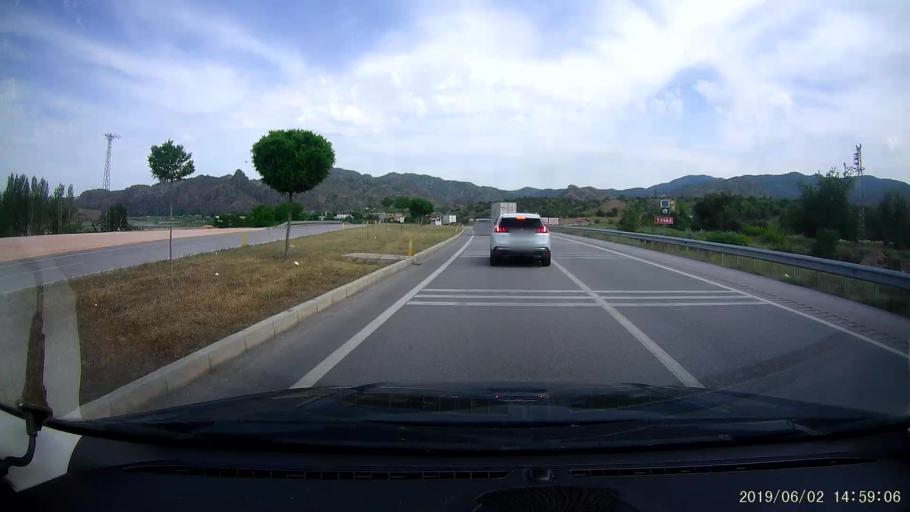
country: TR
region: Corum
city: Osmancik
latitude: 40.9726
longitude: 34.6905
